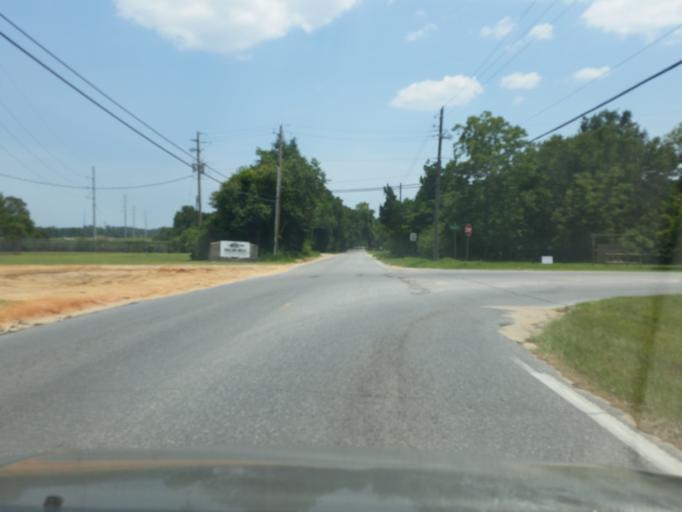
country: US
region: Florida
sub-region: Escambia County
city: Ensley
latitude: 30.4900
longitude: -87.2764
